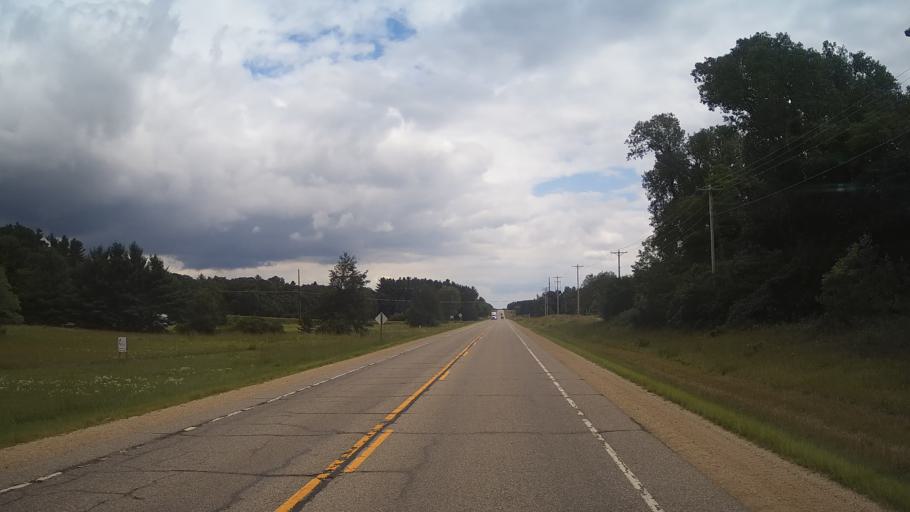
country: US
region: Wisconsin
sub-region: Marquette County
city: Westfield
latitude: 44.0390
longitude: -89.5065
